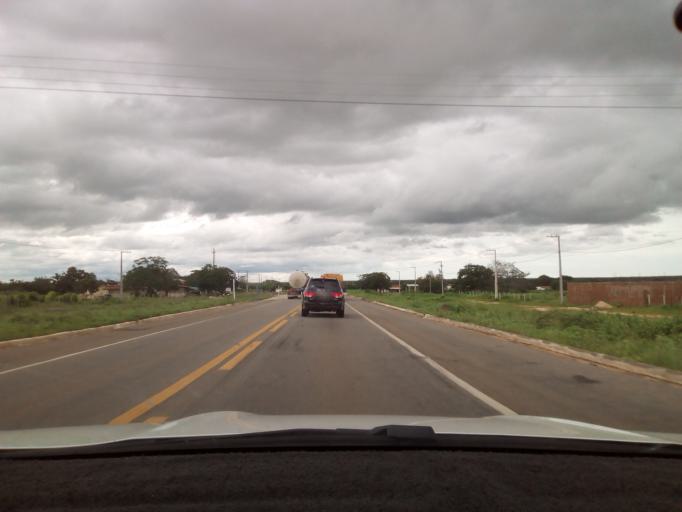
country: BR
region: Rio Grande do Norte
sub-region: Barauna
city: Barauna
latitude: -4.9271
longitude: -37.4172
